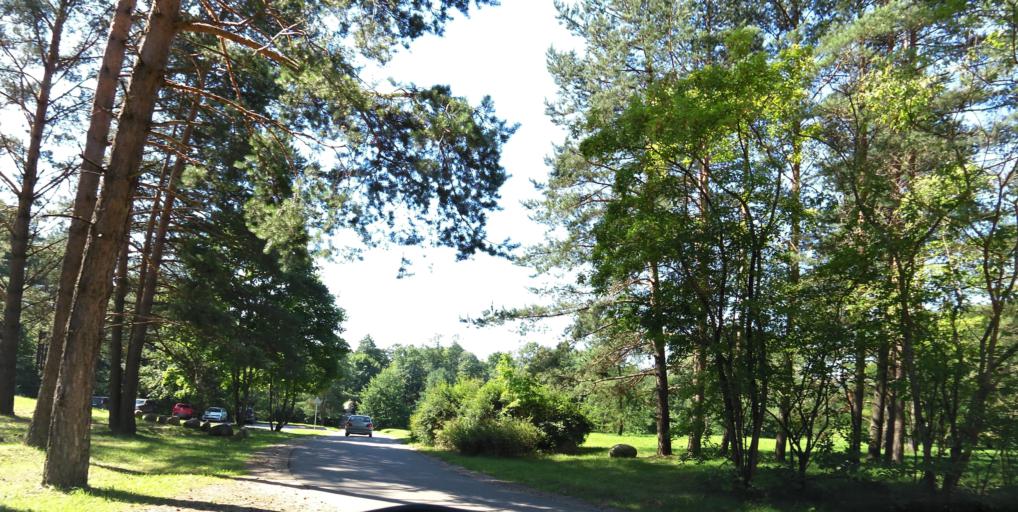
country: LT
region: Vilnius County
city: Rasos
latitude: 54.6894
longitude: 25.3686
